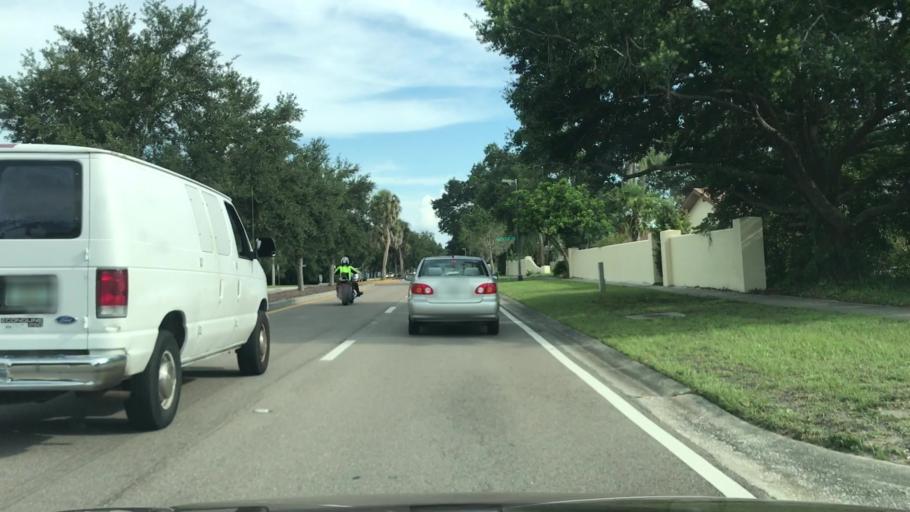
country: US
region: Florida
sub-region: Sarasota County
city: Plantation
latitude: 27.0774
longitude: -82.3890
